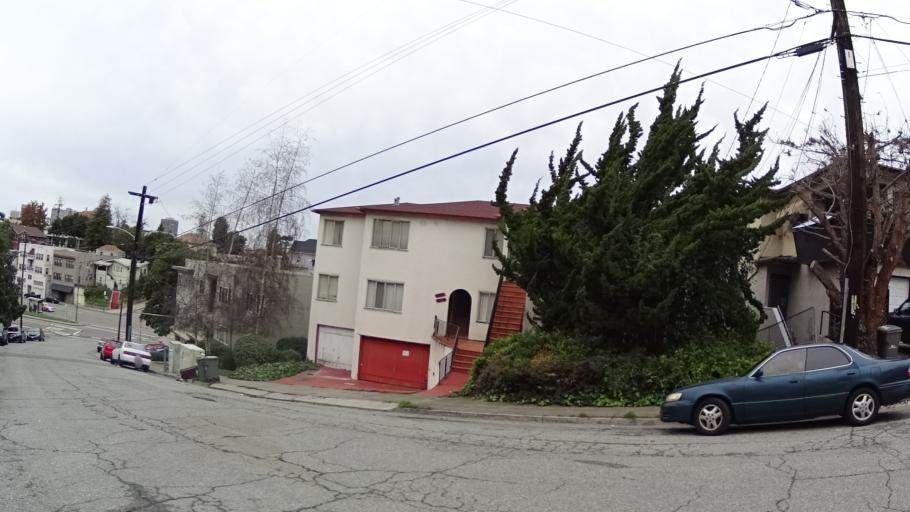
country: US
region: California
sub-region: Alameda County
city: Oakland
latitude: 37.8010
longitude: -122.2452
